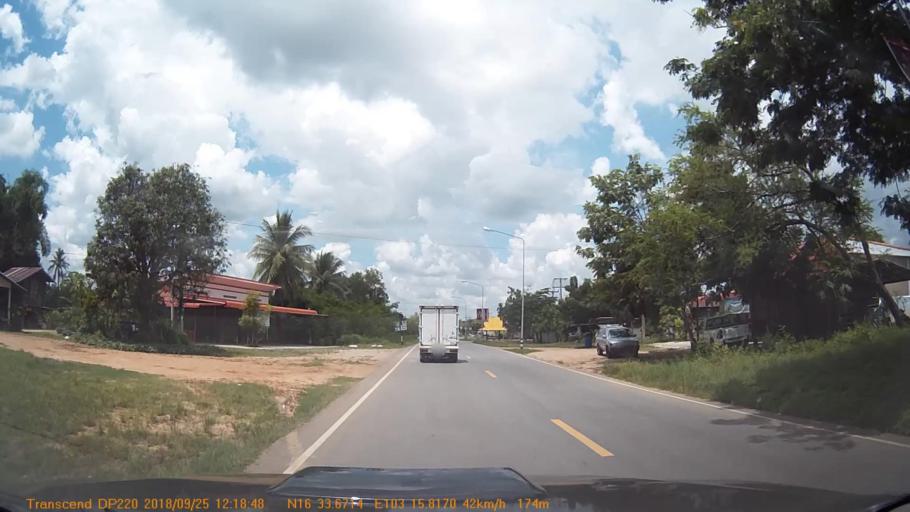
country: TH
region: Kalasin
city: Huai Mek
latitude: 16.5613
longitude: 103.2636
